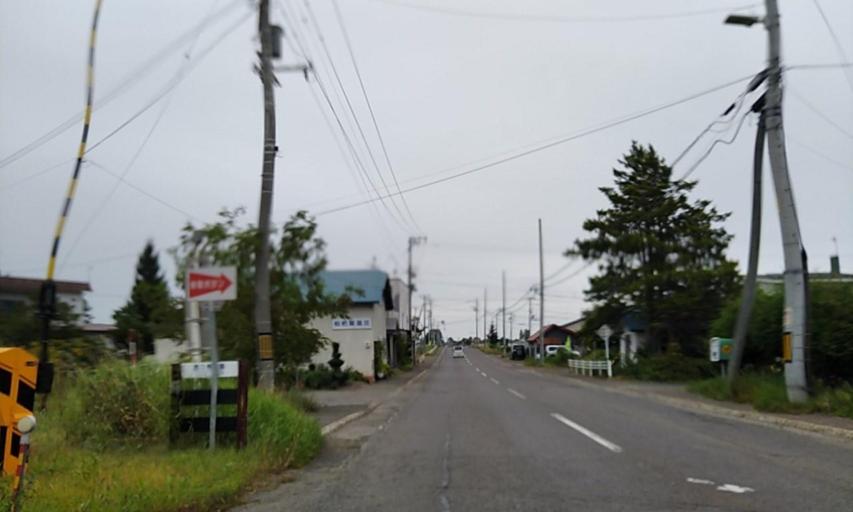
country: JP
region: Hokkaido
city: Bihoro
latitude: 43.8340
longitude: 144.1094
